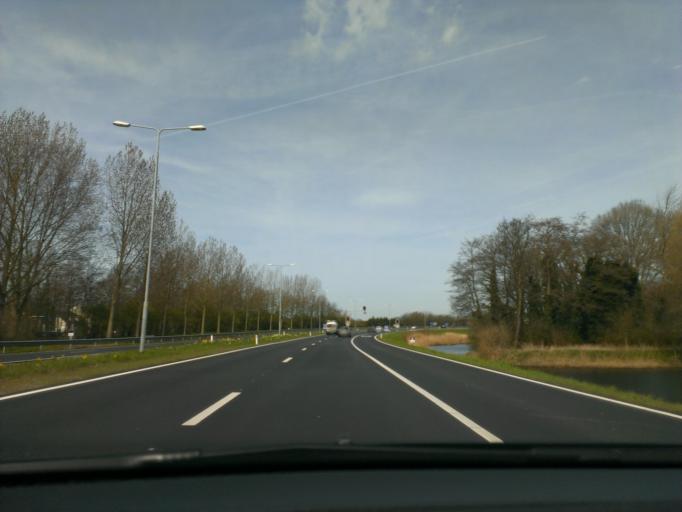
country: NL
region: North Holland
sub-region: Gemeente Heemstede
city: Heemstede
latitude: 52.3342
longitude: 4.6403
